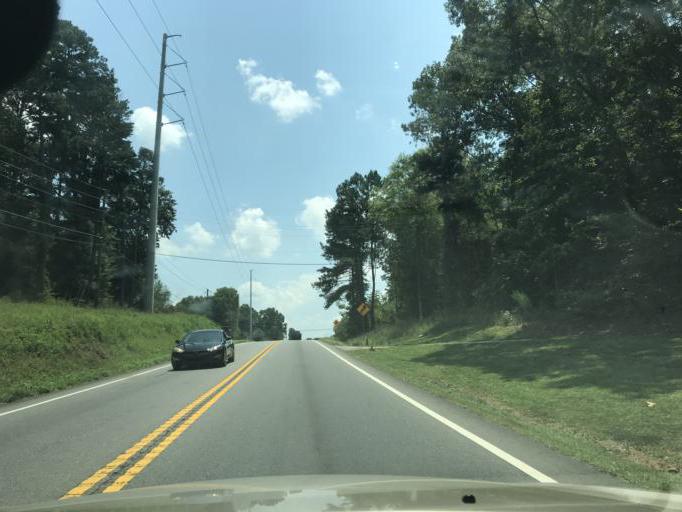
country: US
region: Georgia
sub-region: Forsyth County
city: Cumming
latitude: 34.2851
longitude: -84.1270
